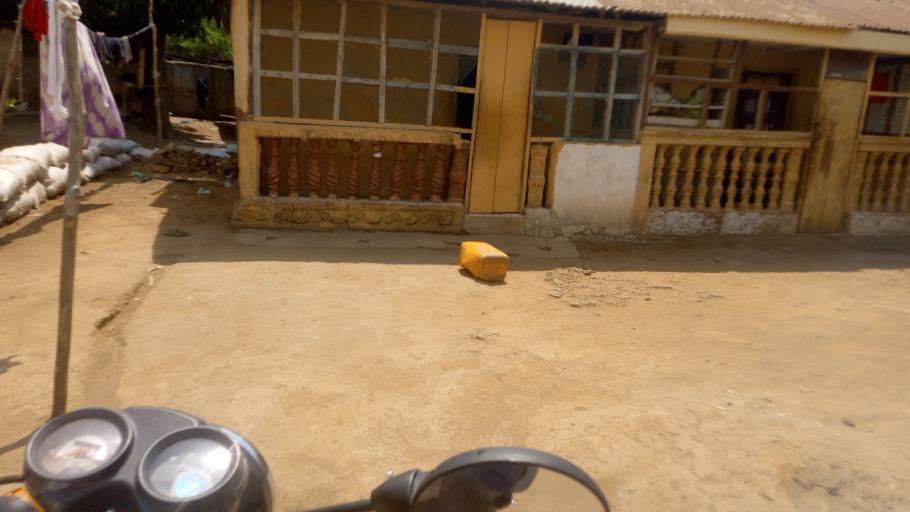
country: SL
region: Western Area
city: Waterloo
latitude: 8.3250
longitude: -13.0746
